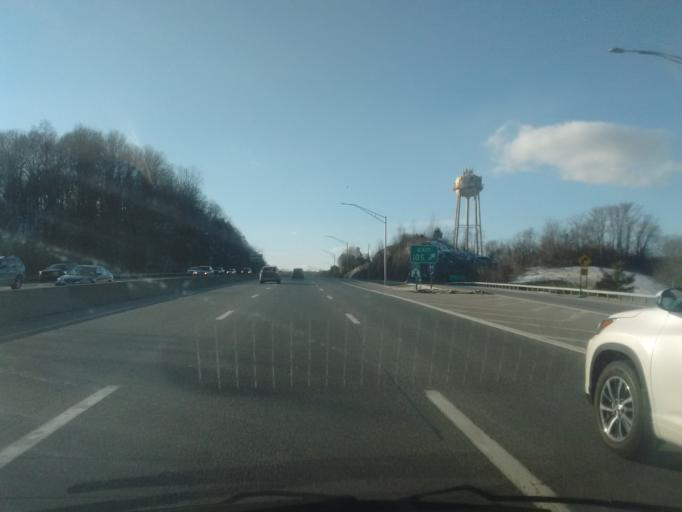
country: US
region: New York
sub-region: Orange County
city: Balmville
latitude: 41.5196
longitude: -74.0228
